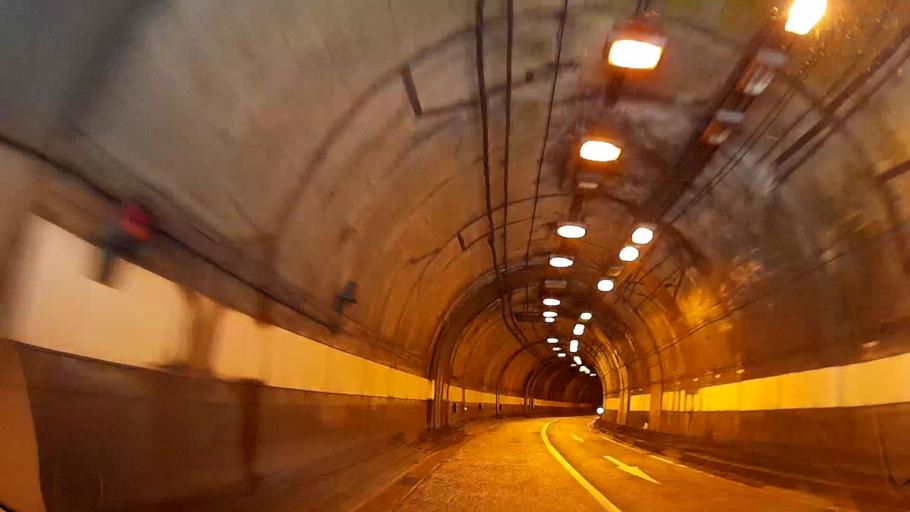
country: JP
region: Nagano
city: Toyoshina
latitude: 36.1523
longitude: 137.6835
